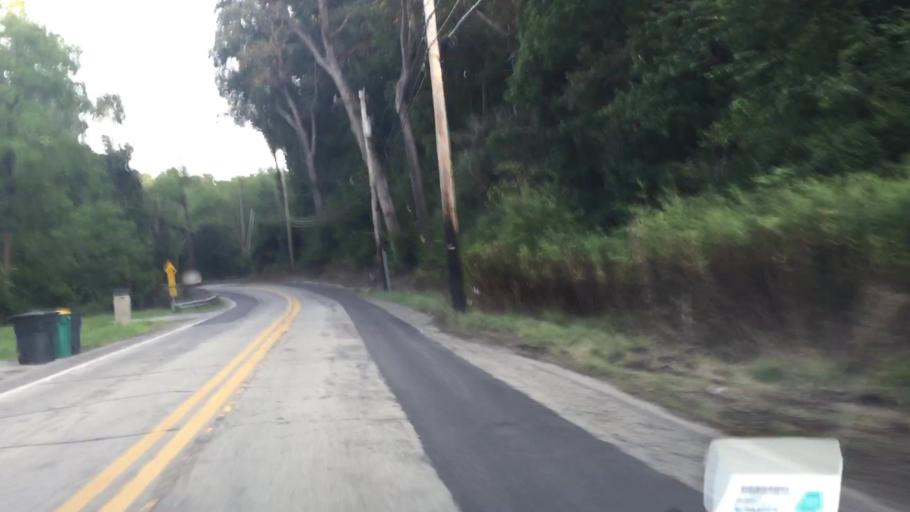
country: US
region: Pennsylvania
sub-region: Allegheny County
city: West View
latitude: 40.5505
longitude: -80.0565
